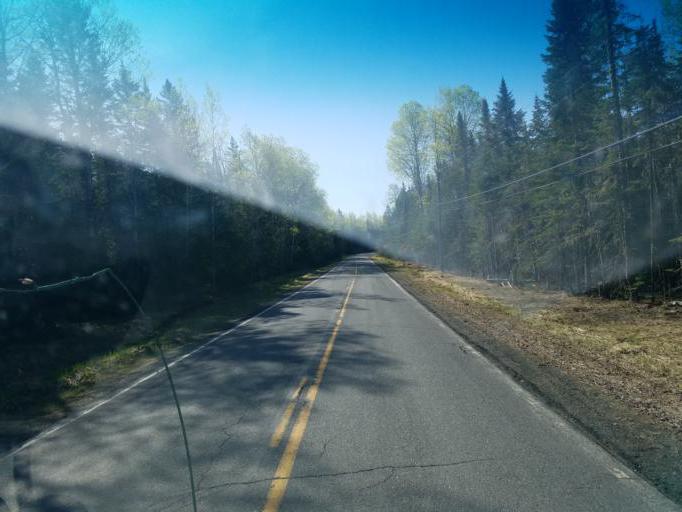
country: US
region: Maine
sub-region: Aroostook County
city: Caribou
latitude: 46.8513
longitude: -68.1988
